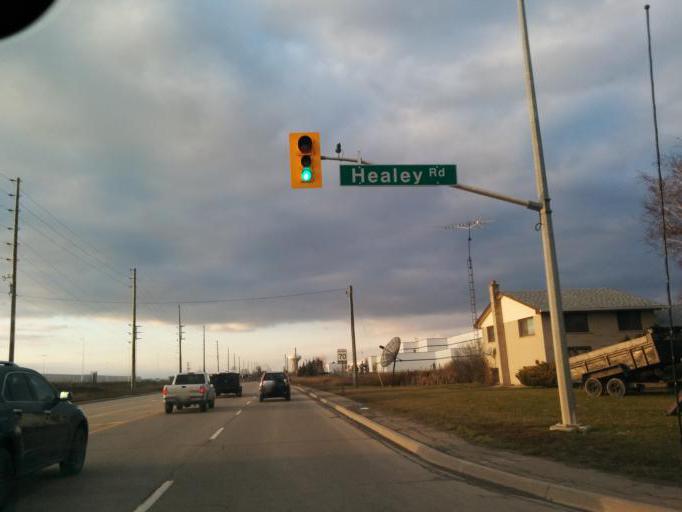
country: CA
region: Ontario
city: Brampton
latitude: 43.8591
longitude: -79.7334
